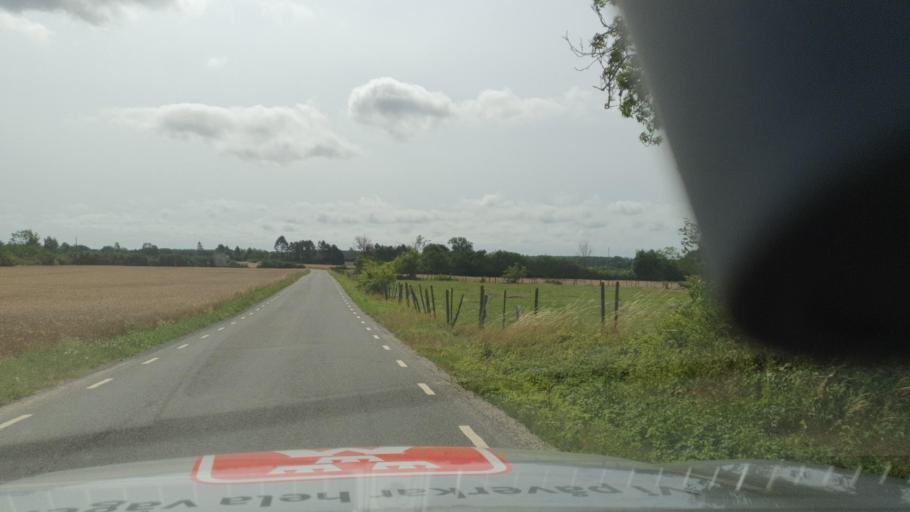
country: SE
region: Skane
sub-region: Kristianstads Kommun
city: Fjalkinge
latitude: 56.0631
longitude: 14.3660
